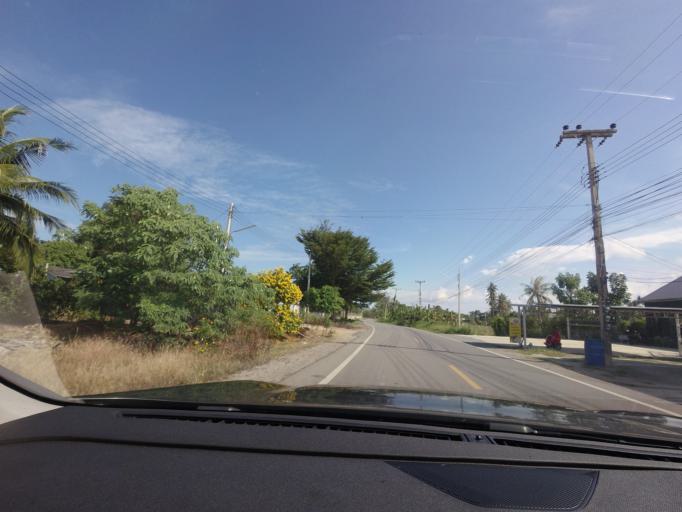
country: TH
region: Prachuap Khiri Khan
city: Pran Buri
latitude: 12.4416
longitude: 99.9451
